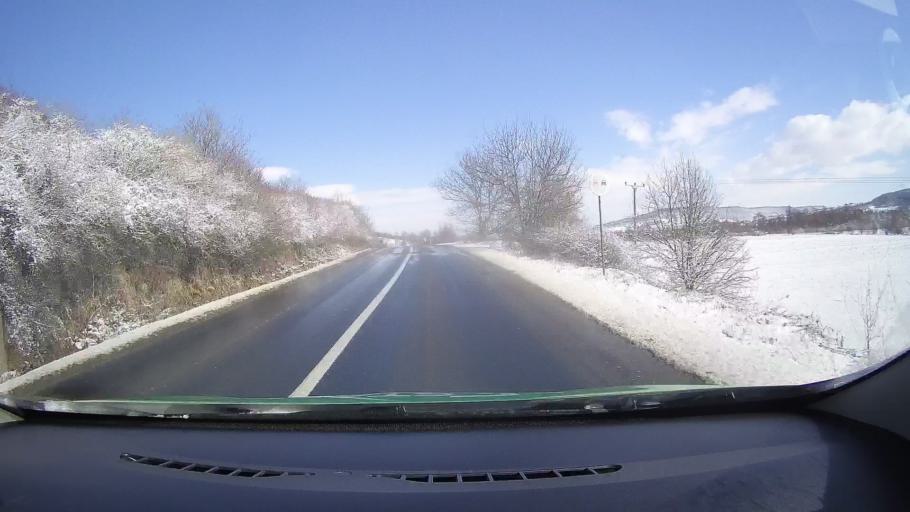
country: RO
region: Sibiu
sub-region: Comuna Rosia
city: Rosia
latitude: 45.8315
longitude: 24.3968
